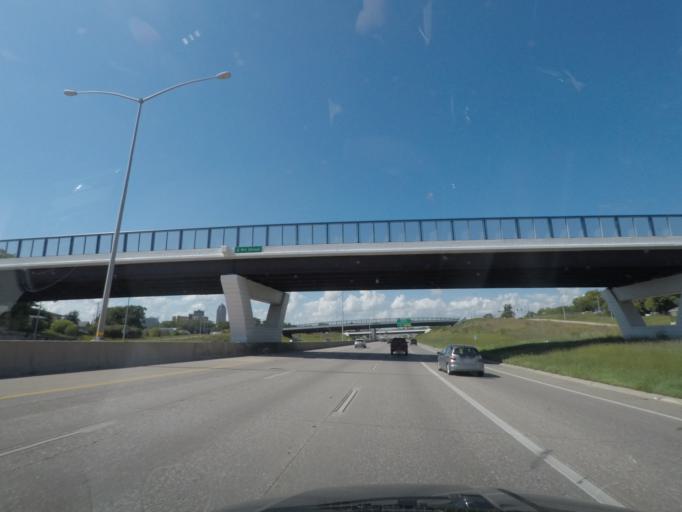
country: US
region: Iowa
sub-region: Polk County
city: Des Moines
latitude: 41.5951
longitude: -93.6060
